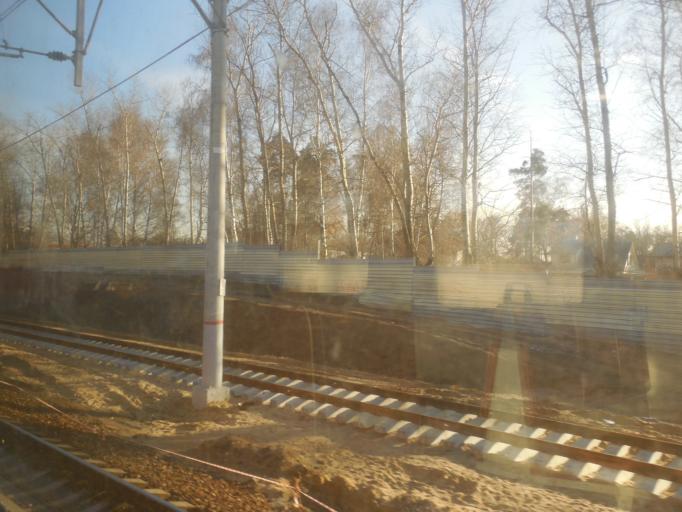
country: RU
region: Moskovskaya
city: Saltykovka
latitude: 55.7559
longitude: 37.9335
